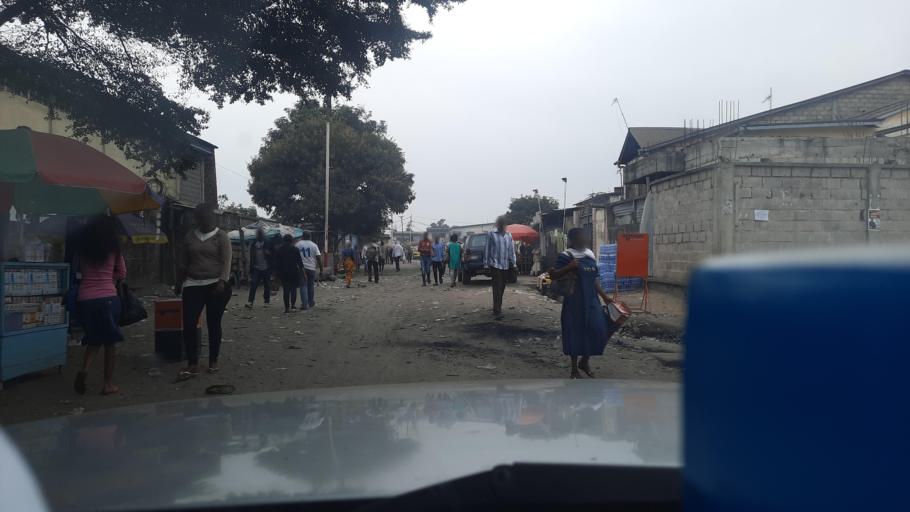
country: CD
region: Kinshasa
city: Masina
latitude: -4.3898
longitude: 15.3481
